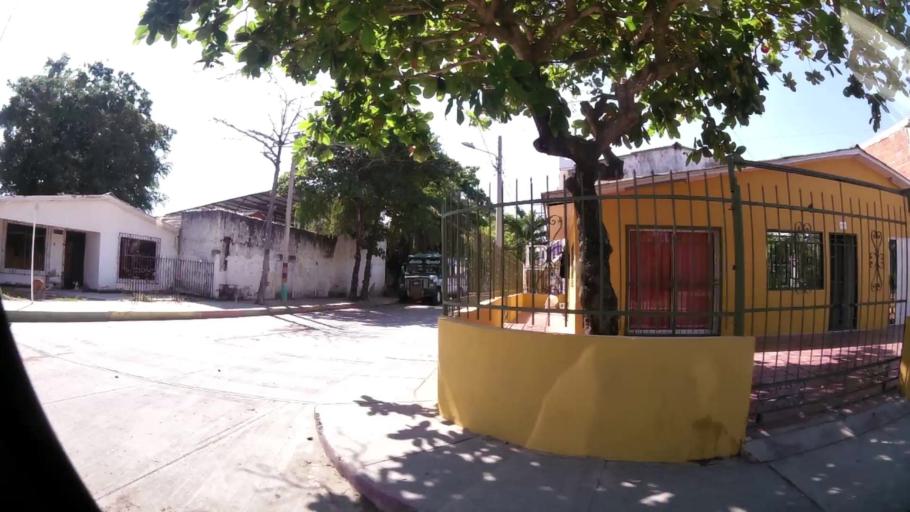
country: CO
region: Bolivar
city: Cartagena
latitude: 10.4419
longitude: -75.5221
